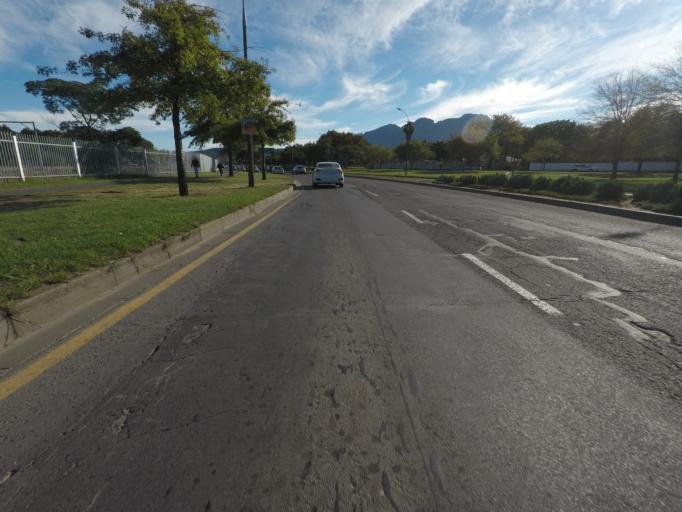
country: ZA
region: Western Cape
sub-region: Cape Winelands District Municipality
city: Stellenbosch
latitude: -33.9361
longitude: 18.8519
